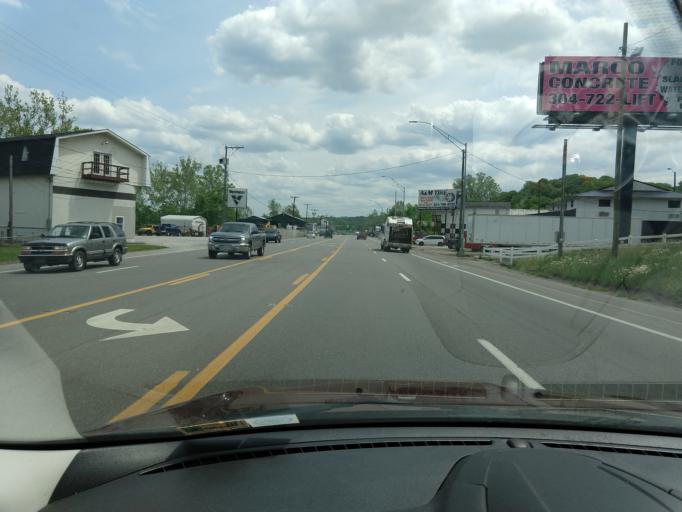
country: US
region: West Virginia
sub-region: Kanawha County
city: Dunbar
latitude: 38.3582
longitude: -81.7560
